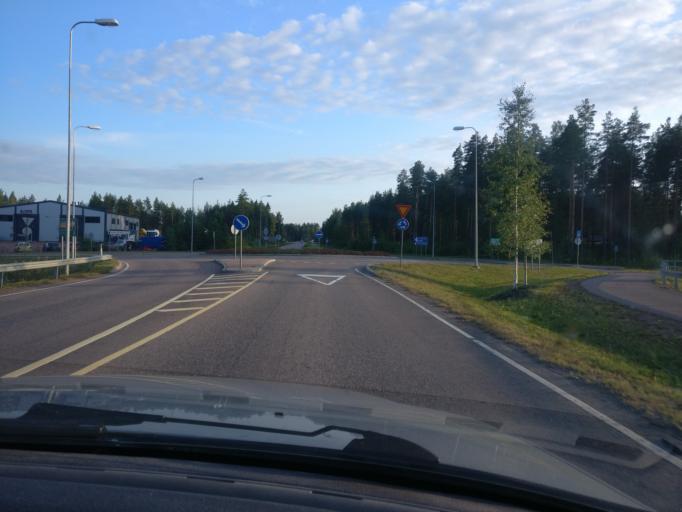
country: FI
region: Kymenlaakso
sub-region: Kotka-Hamina
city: Broby
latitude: 60.5019
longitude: 26.7418
